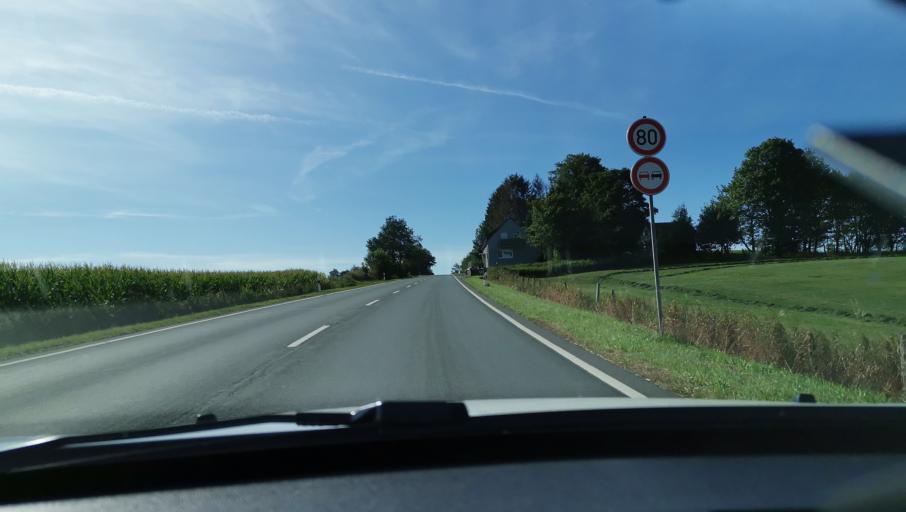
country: DE
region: North Rhine-Westphalia
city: Halver
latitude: 51.2132
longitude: 7.4875
